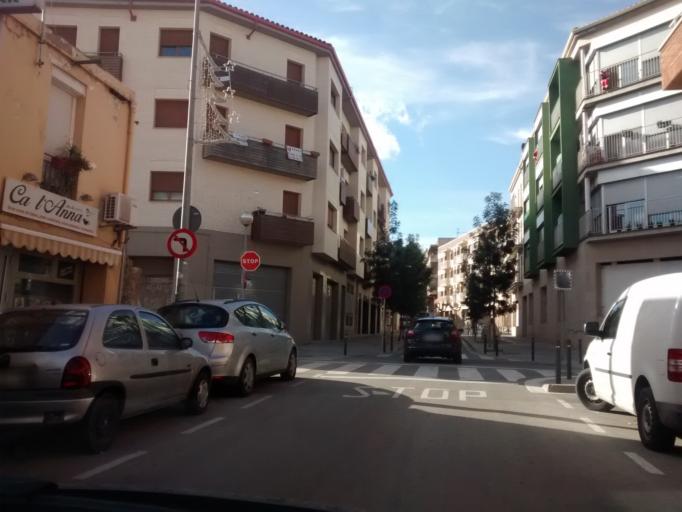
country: ES
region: Catalonia
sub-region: Provincia de Barcelona
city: Sant Vicenc dels Horts
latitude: 41.3960
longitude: 2.0102
